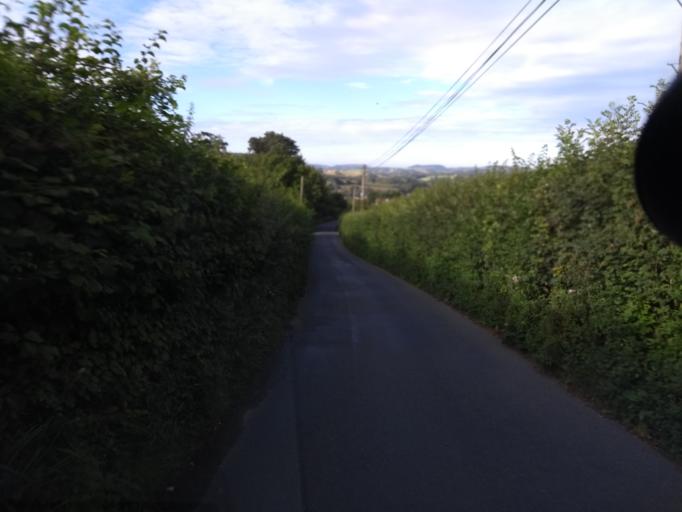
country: GB
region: England
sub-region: Dorset
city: Beaminster
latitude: 50.8163
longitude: -2.7240
